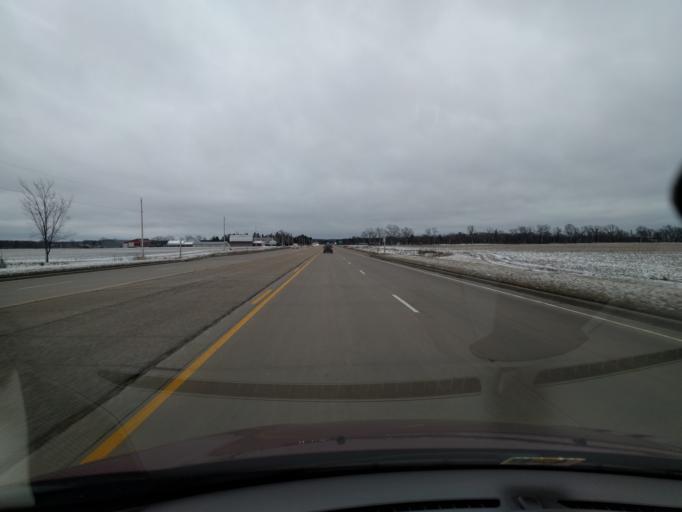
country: US
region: Wisconsin
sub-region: Portage County
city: Whiting
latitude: 44.5230
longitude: -89.4821
